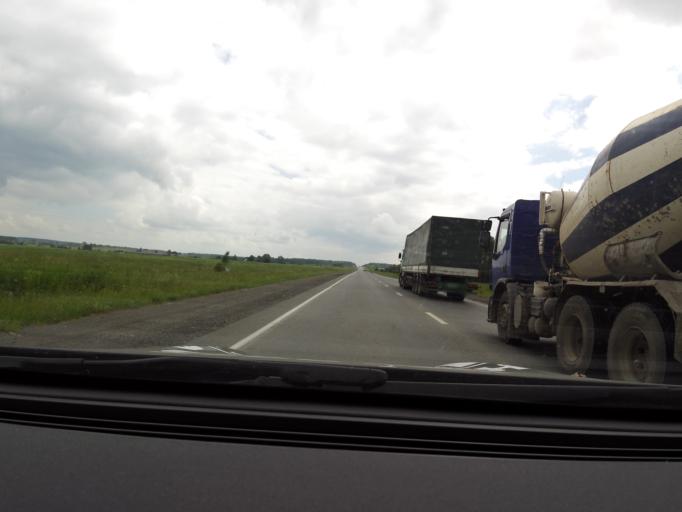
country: RU
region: Perm
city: Orda
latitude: 57.2988
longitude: 56.9860
